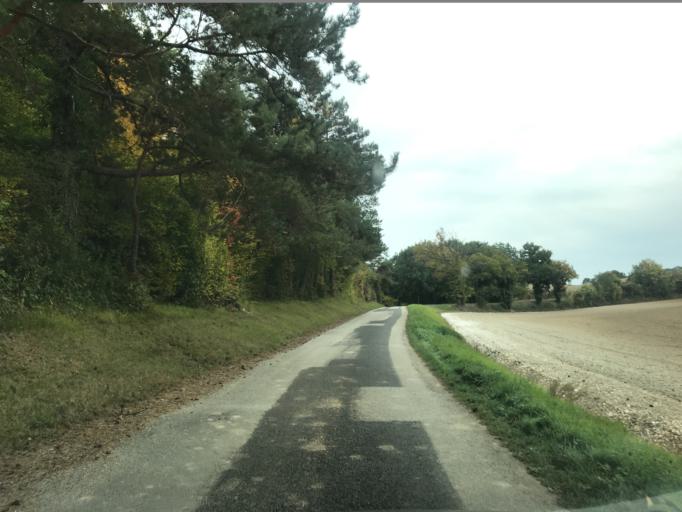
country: FR
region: Haute-Normandie
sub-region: Departement de l'Eure
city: Heudreville-sur-Eure
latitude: 49.0980
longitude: 1.2239
